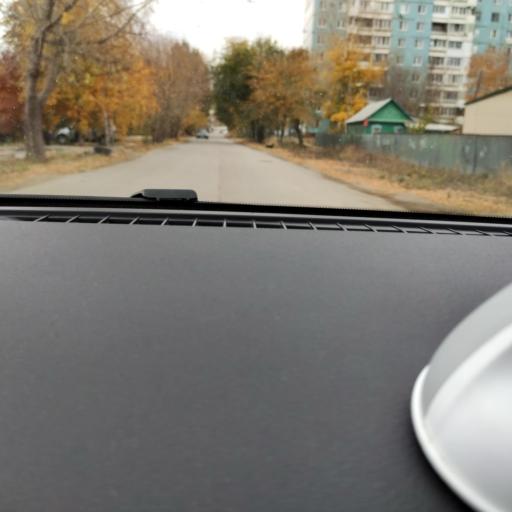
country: RU
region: Samara
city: Petra-Dubrava
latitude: 53.2431
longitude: 50.3137
